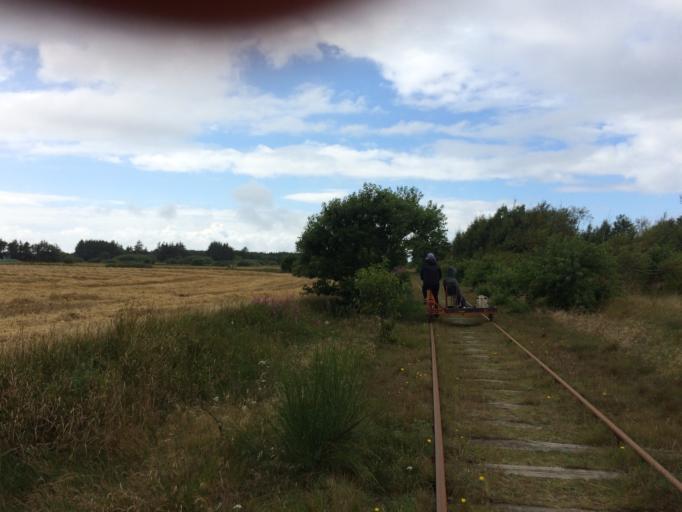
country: DK
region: South Denmark
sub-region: Varde Kommune
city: Oksbol
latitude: 55.7829
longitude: 8.2669
